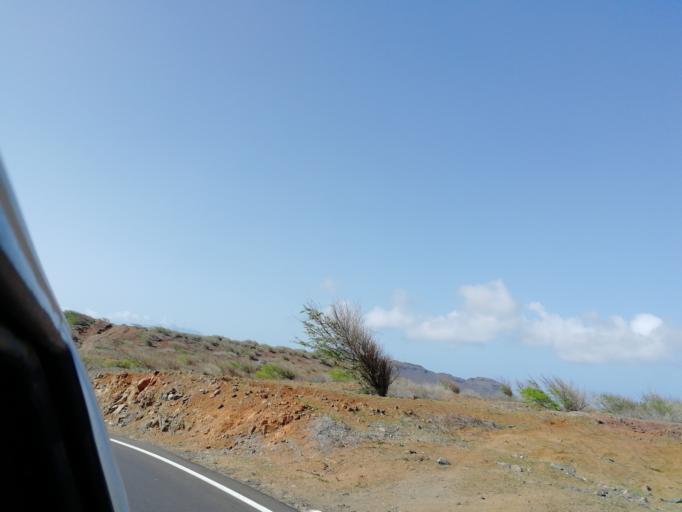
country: CV
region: Sao Vicente
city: Mindelo
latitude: 16.8768
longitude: -24.9458
